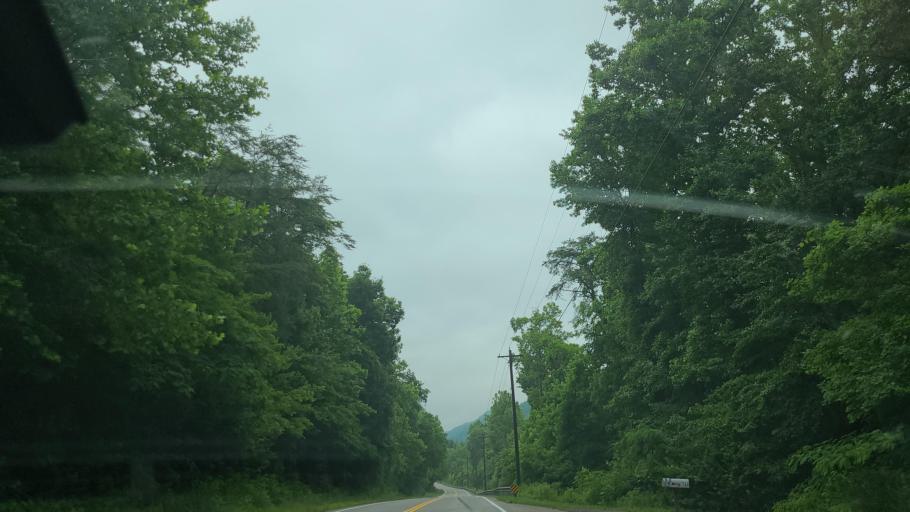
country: US
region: Tennessee
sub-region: Anderson County
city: Oak Ridge
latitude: 36.0975
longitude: -84.2553
